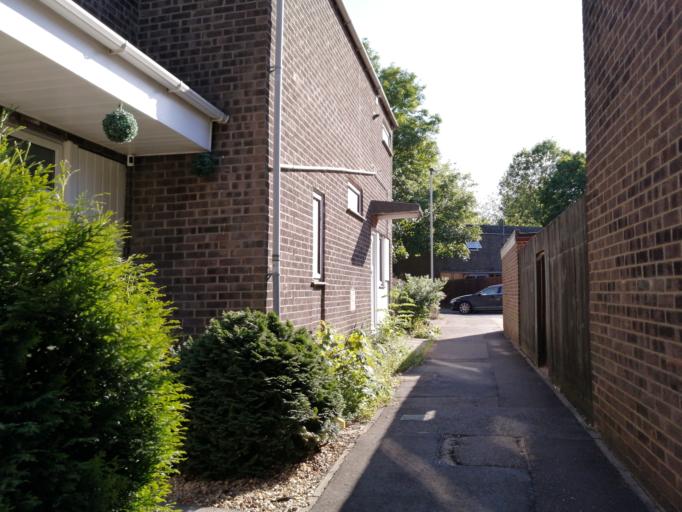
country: GB
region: England
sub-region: Peterborough
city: Peterborough
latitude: 52.5932
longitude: -0.2736
